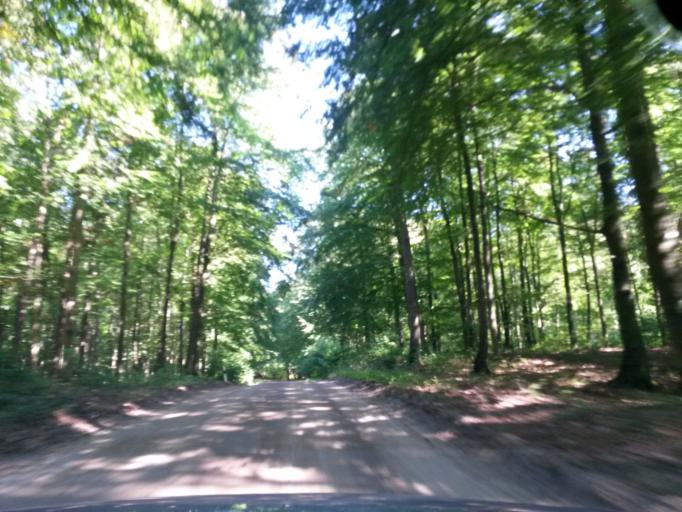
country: DE
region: Brandenburg
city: Templin
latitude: 53.1953
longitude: 13.4520
